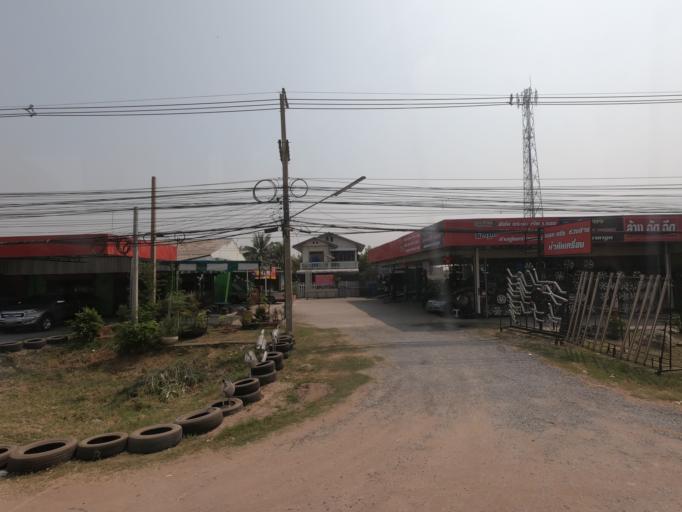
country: TH
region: Nakhon Ratchasima
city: Nakhon Ratchasima
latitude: 15.0400
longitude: 102.1481
